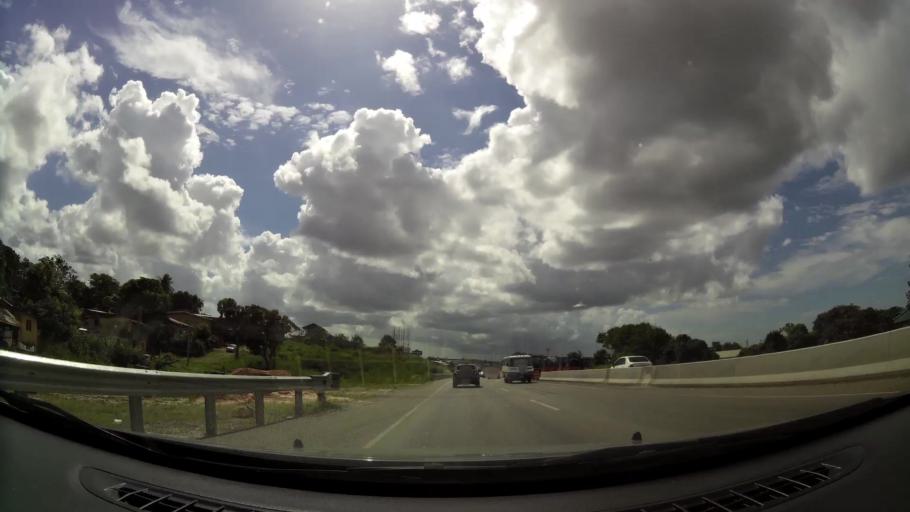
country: TT
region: City of San Fernando
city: San Fernando
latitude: 10.2518
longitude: -61.4841
